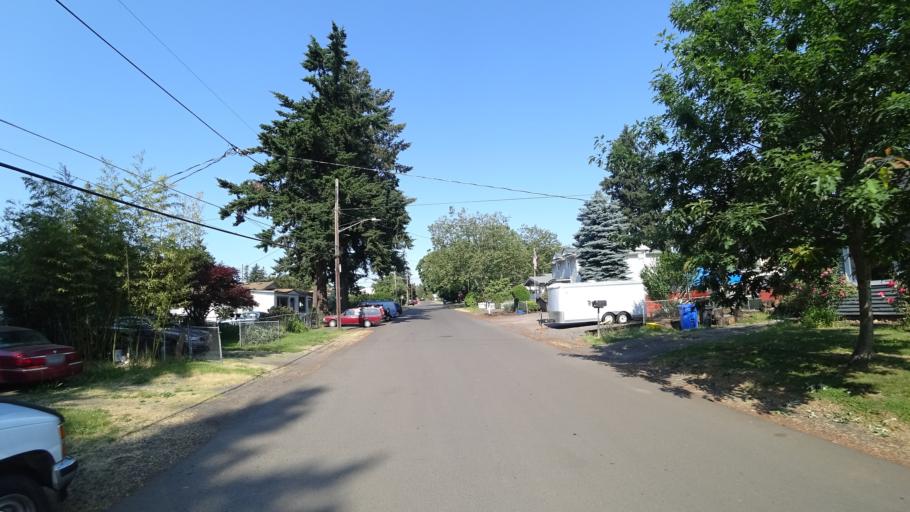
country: US
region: Oregon
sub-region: Multnomah County
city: Lents
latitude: 45.4608
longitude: -122.5909
